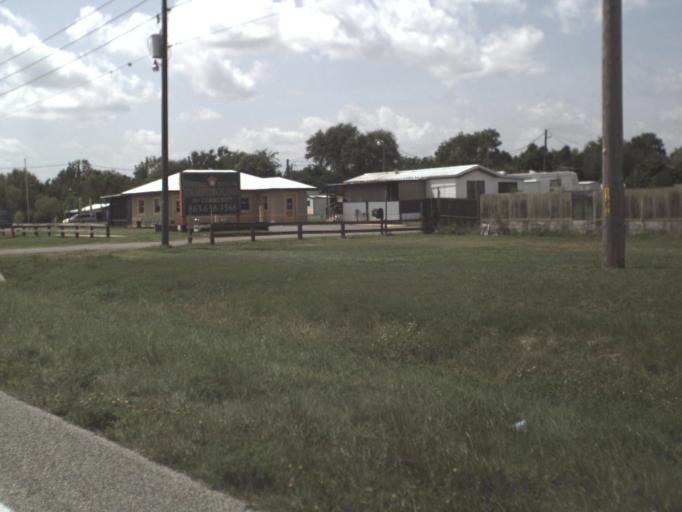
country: US
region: Florida
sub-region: Polk County
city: Crooked Lake Park
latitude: 27.8493
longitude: -81.5856
